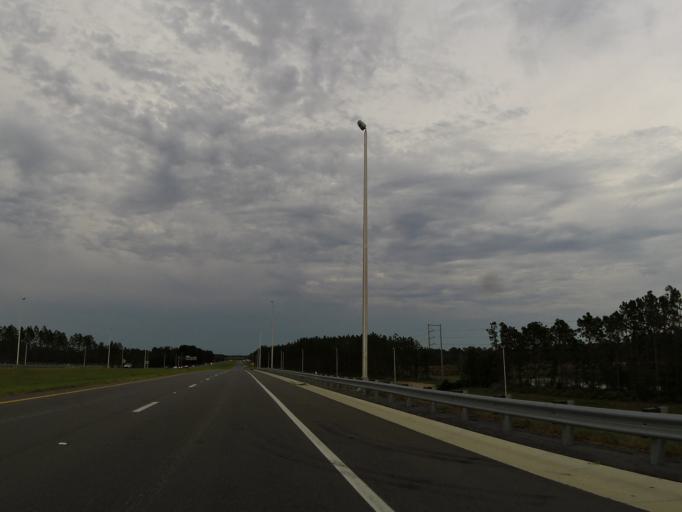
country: US
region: Florida
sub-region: Clay County
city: Bellair-Meadowbrook Terrace
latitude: 30.1970
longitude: -81.8373
